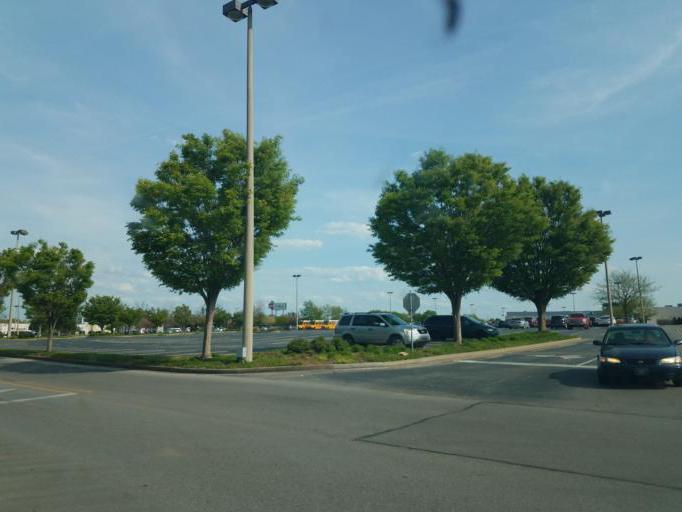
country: US
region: Kentucky
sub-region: Warren County
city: Bowling Green
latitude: 36.9511
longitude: -86.4281
